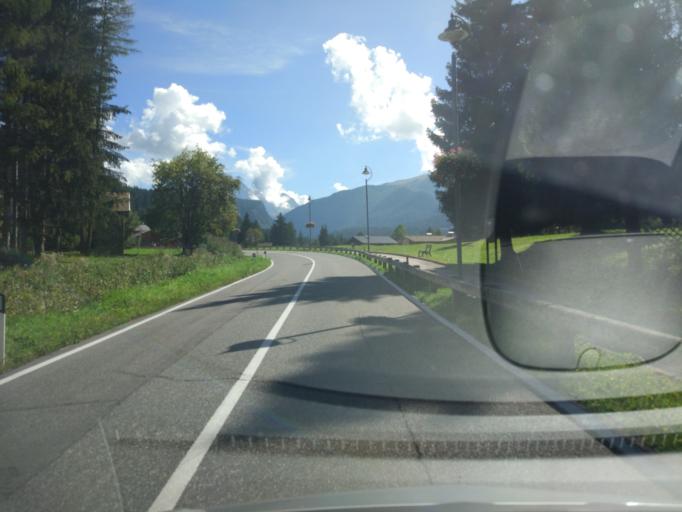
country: IT
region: Trentino-Alto Adige
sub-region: Provincia di Trento
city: Moena
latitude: 46.3111
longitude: 11.6725
